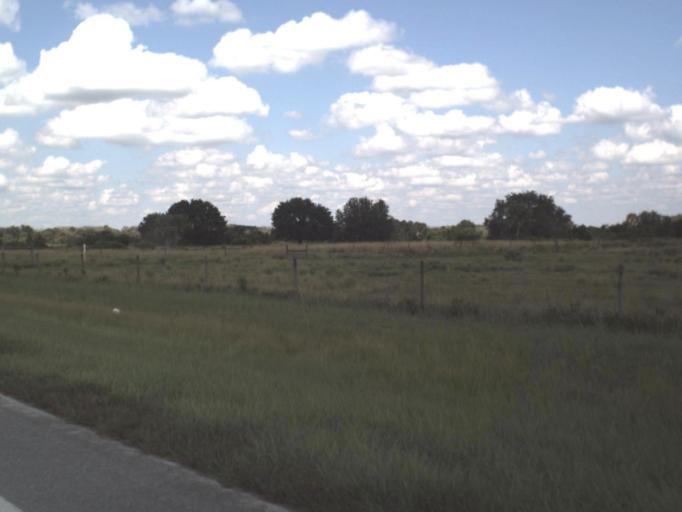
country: US
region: Florida
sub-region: Highlands County
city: Lake Placid
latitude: 27.4171
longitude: -81.1982
